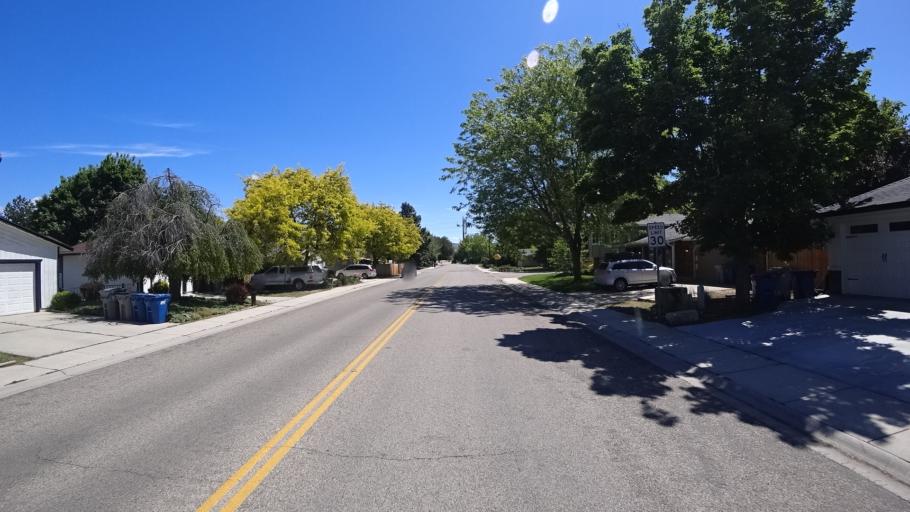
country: US
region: Idaho
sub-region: Ada County
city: Boise
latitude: 43.5678
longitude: -116.1612
